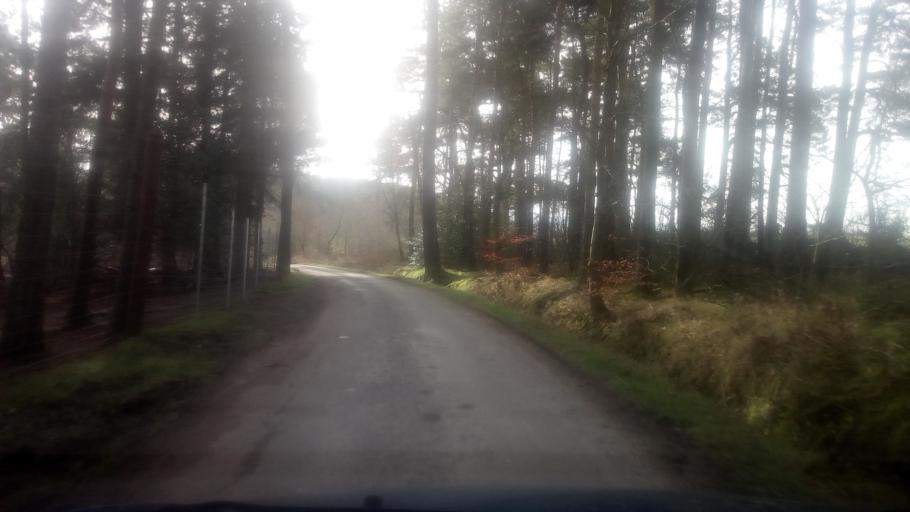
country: GB
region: Scotland
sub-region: The Scottish Borders
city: Jedburgh
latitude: 55.4294
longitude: -2.6411
